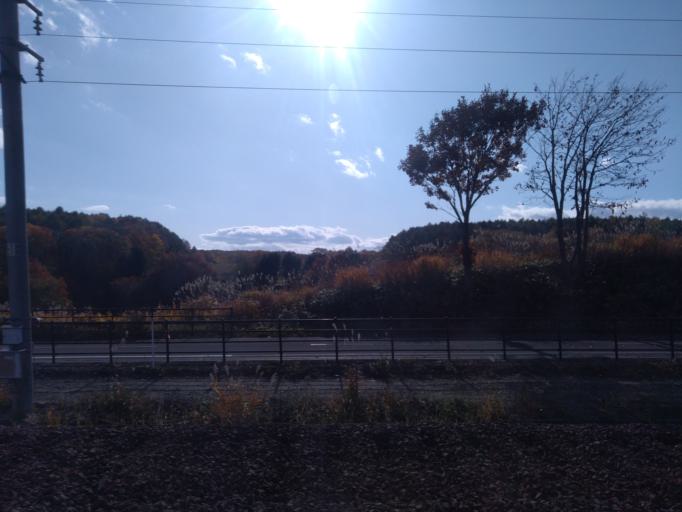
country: JP
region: Hokkaido
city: Kitahiroshima
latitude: 42.9975
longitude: 141.5327
